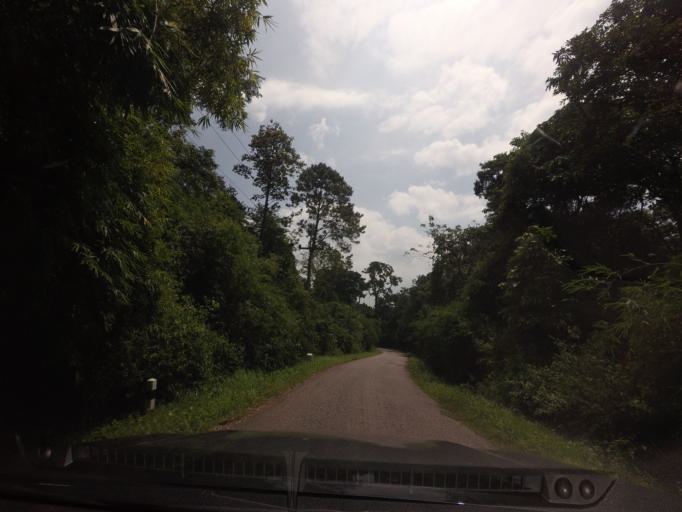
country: TH
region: Loei
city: Phu Ruea
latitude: 17.4678
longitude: 101.3552
